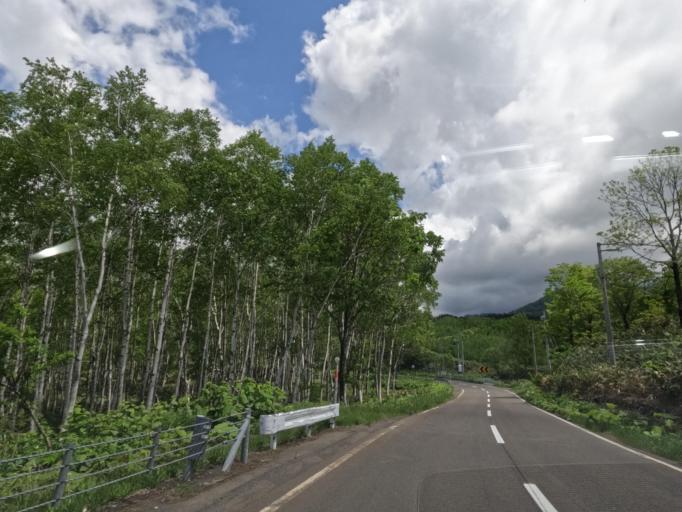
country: JP
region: Hokkaido
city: Takikawa
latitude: 43.5417
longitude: 141.6451
